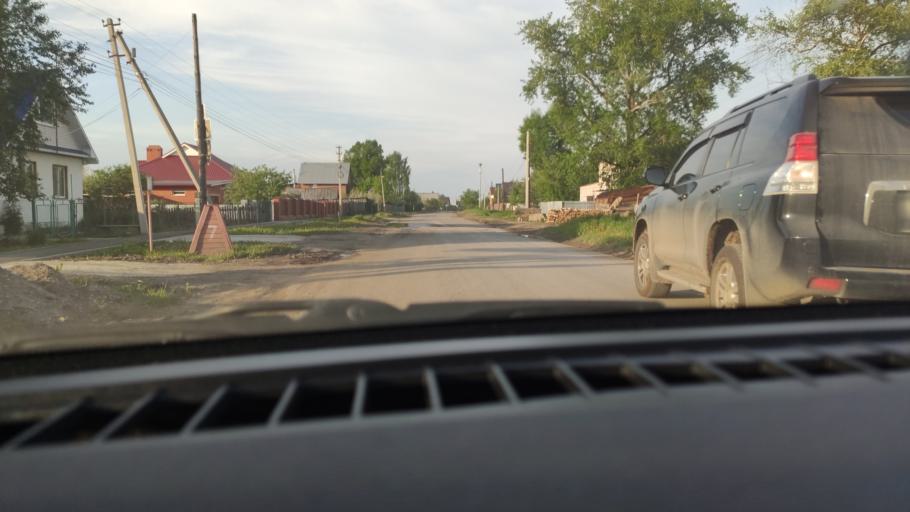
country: RU
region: Perm
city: Kultayevo
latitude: 57.9331
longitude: 56.0193
